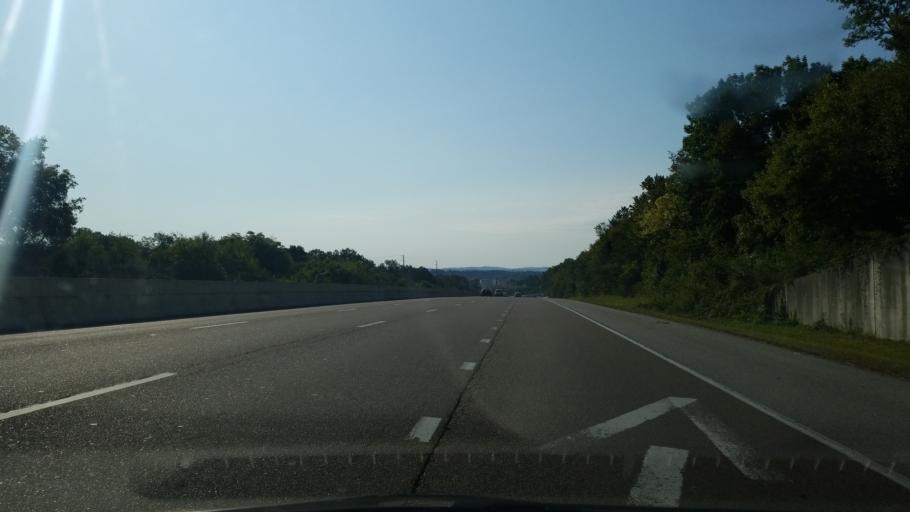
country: US
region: Tennessee
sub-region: Hamilton County
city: East Chattanooga
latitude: 35.0808
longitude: -85.2049
